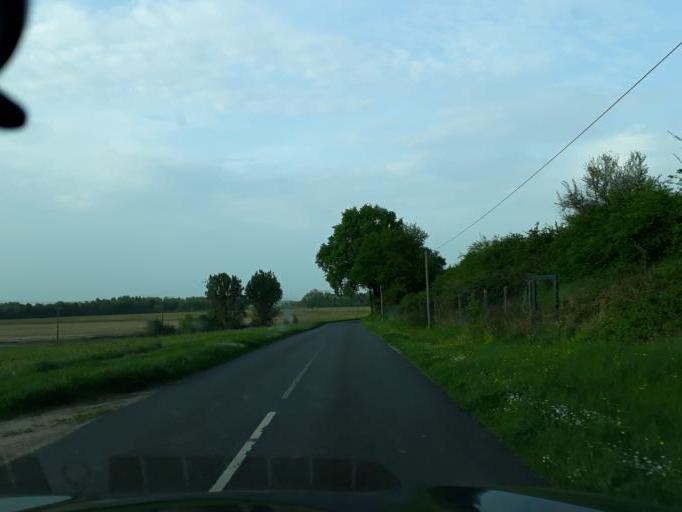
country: FR
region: Centre
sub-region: Departement du Loiret
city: Tavers
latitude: 47.7307
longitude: 1.6369
